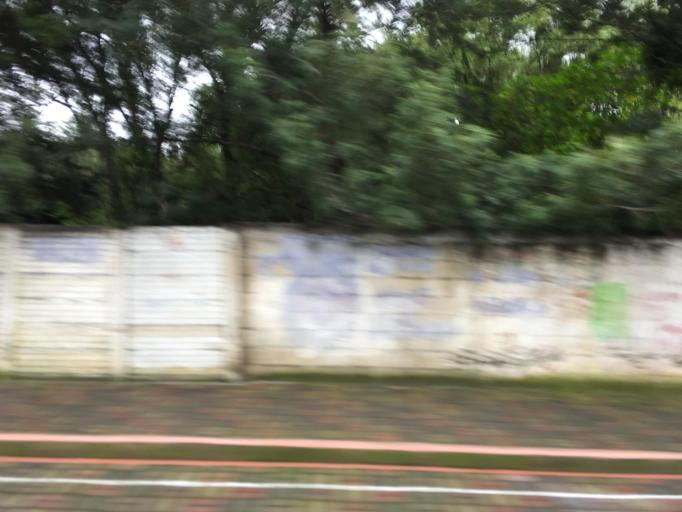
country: GT
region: Sacatepequez
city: Pastores
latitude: 14.5979
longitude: -90.7560
